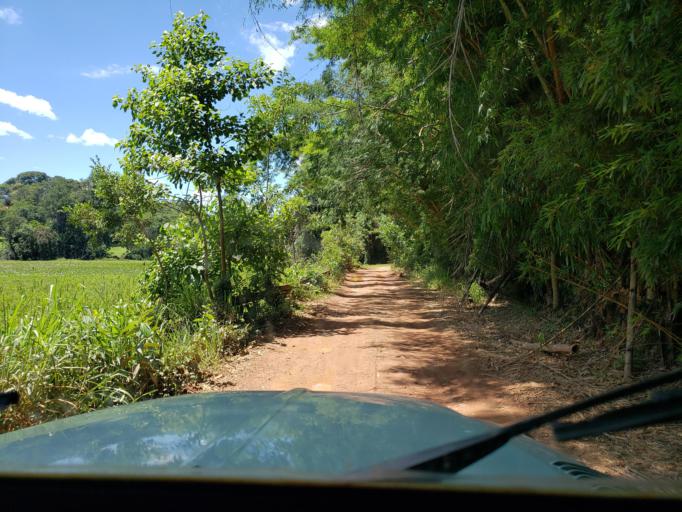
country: BR
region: Sao Paulo
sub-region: Moji-Guacu
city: Mogi-Gaucu
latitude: -22.3120
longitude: -46.8785
